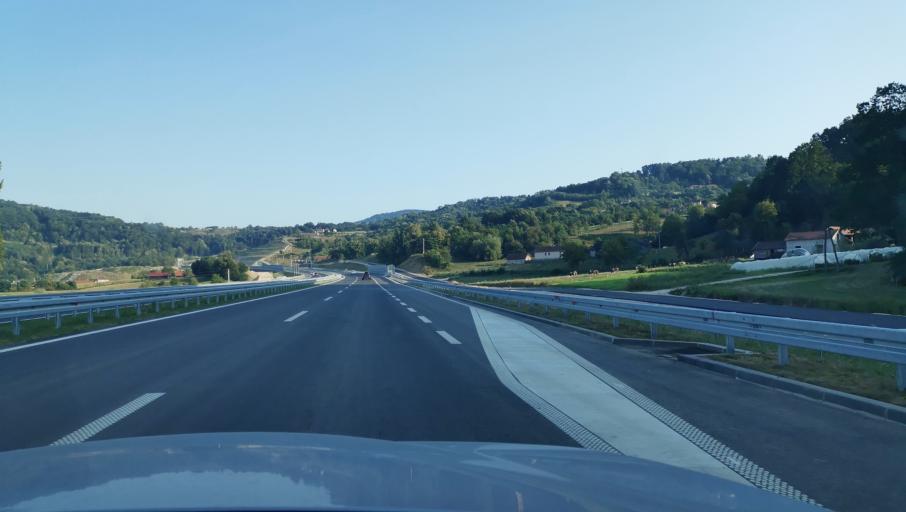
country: RS
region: Central Serbia
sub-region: Kolubarski Okrug
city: Ljig
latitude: 44.2225
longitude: 20.2553
